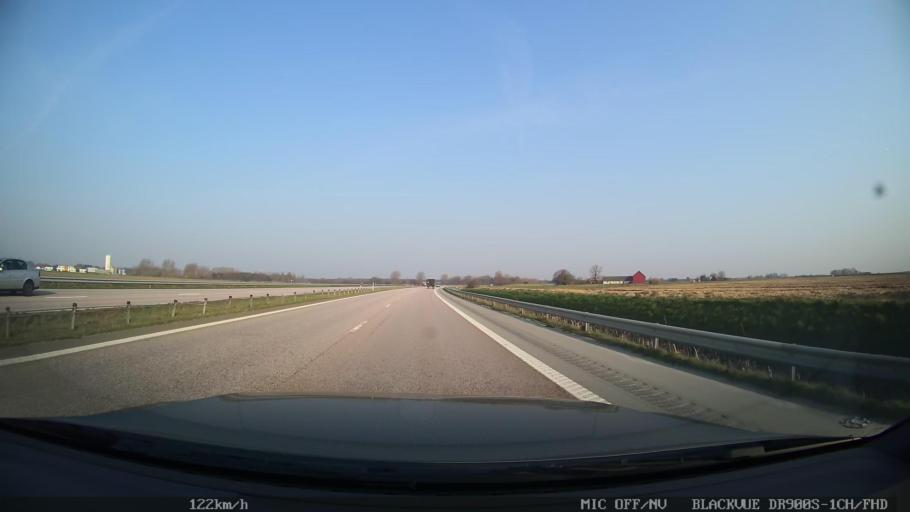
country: SE
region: Skane
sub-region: Kavlinge Kommun
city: Hofterup
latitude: 55.7739
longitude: 12.9754
